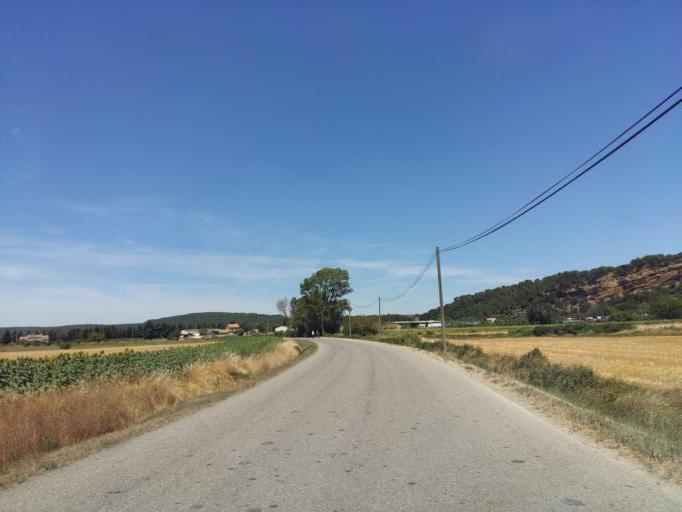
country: FR
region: Provence-Alpes-Cote d'Azur
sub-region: Departement du Vaucluse
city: Piolenc
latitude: 44.1685
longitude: 4.7554
